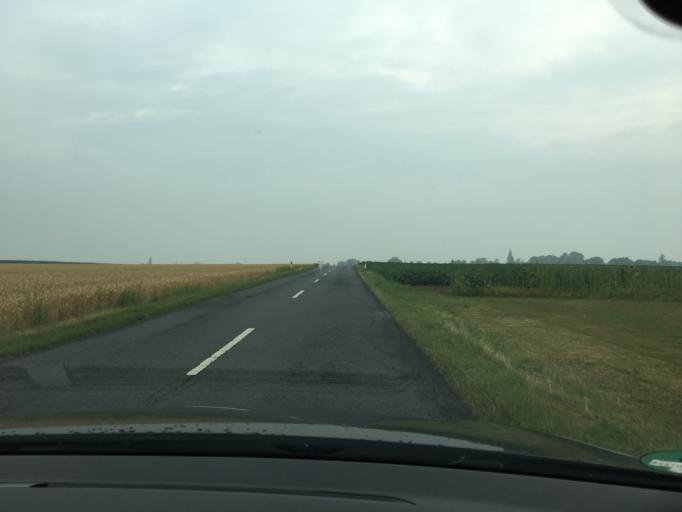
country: DE
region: North Rhine-Westphalia
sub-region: Regierungsbezirk Koln
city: Titz
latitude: 50.9700
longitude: 6.4110
